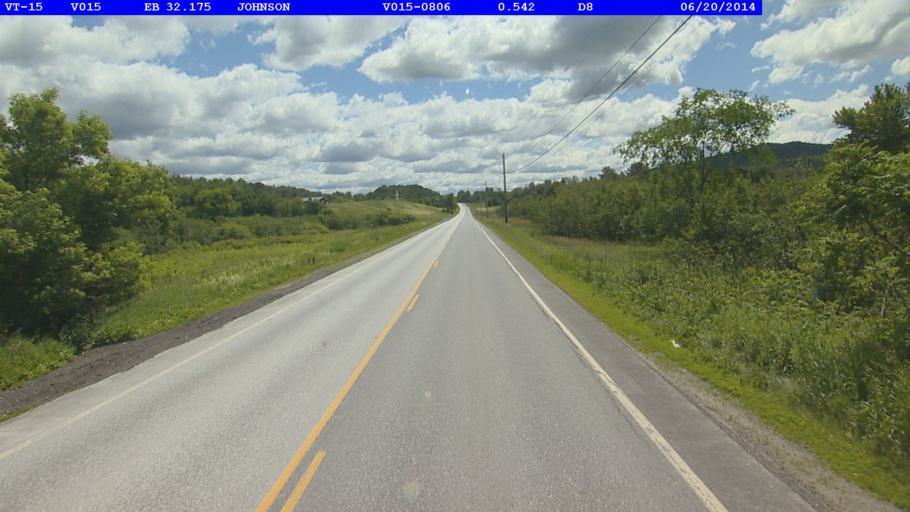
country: US
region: Vermont
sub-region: Lamoille County
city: Johnson
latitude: 44.6490
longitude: -72.7438
